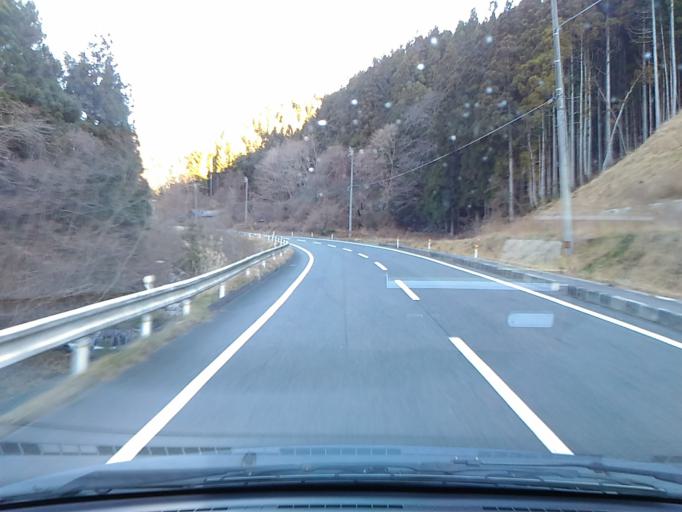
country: JP
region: Ibaraki
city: Kitaibaraki
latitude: 36.9494
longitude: 140.6277
